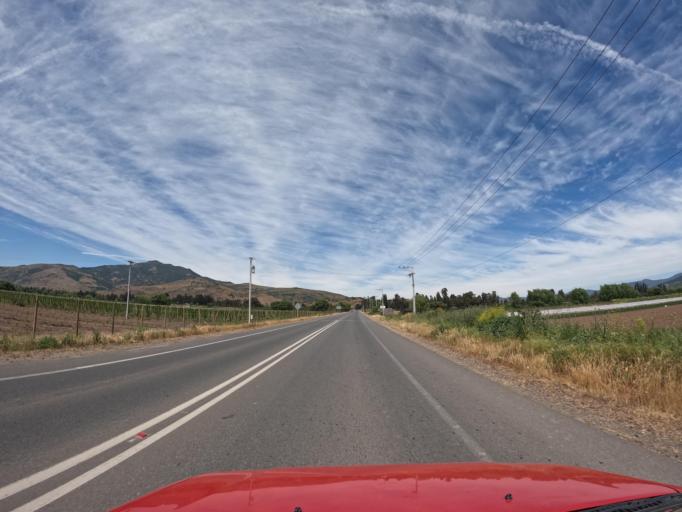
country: CL
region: Maule
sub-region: Provincia de Talca
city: Talca
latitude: -35.1018
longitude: -71.6347
